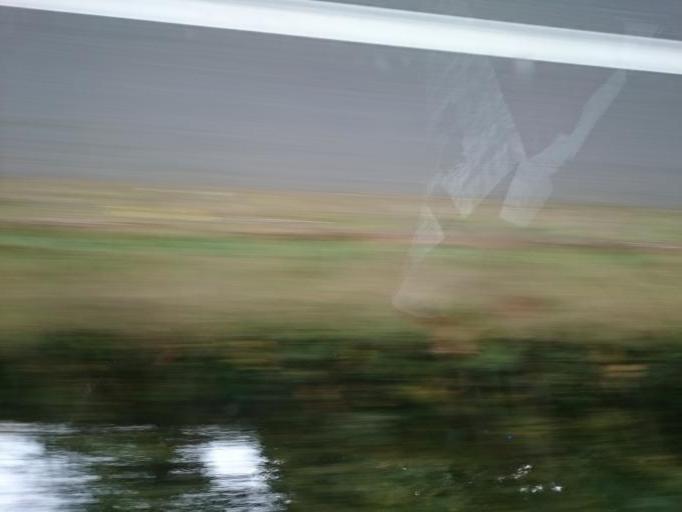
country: FR
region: Brittany
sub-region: Departement d'Ille-et-Vilaine
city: Montauban-de-Bretagne
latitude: 48.2139
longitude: -2.0902
